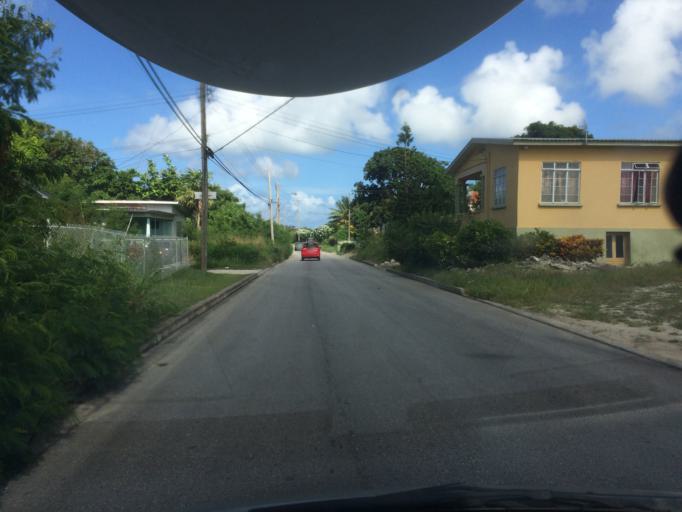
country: BB
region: Saint Lucy
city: Checker Hall
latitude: 13.2872
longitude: -59.6401
